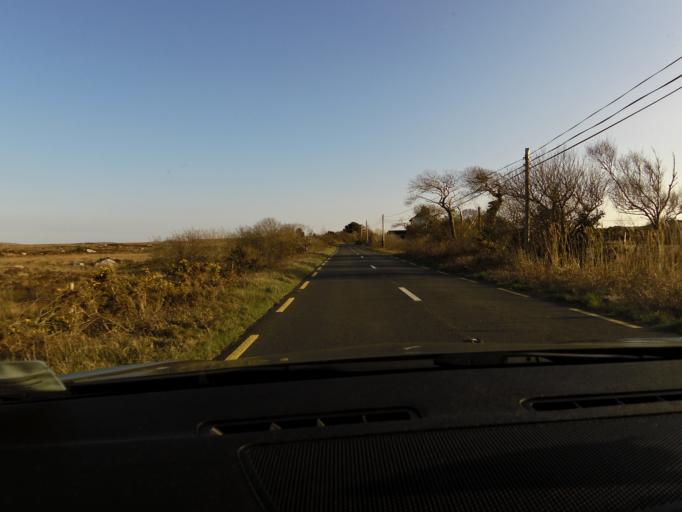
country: IE
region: Connaught
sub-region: County Galway
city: Oughterard
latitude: 53.3736
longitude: -9.5443
